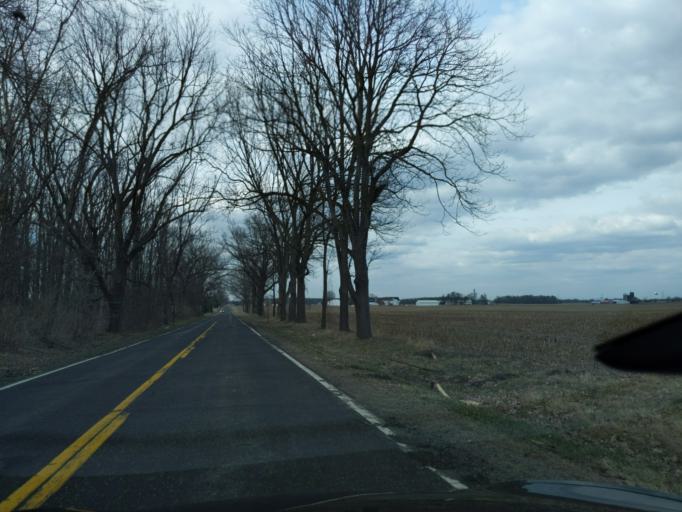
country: US
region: Michigan
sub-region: Ingham County
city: Mason
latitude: 42.5749
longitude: -84.4834
